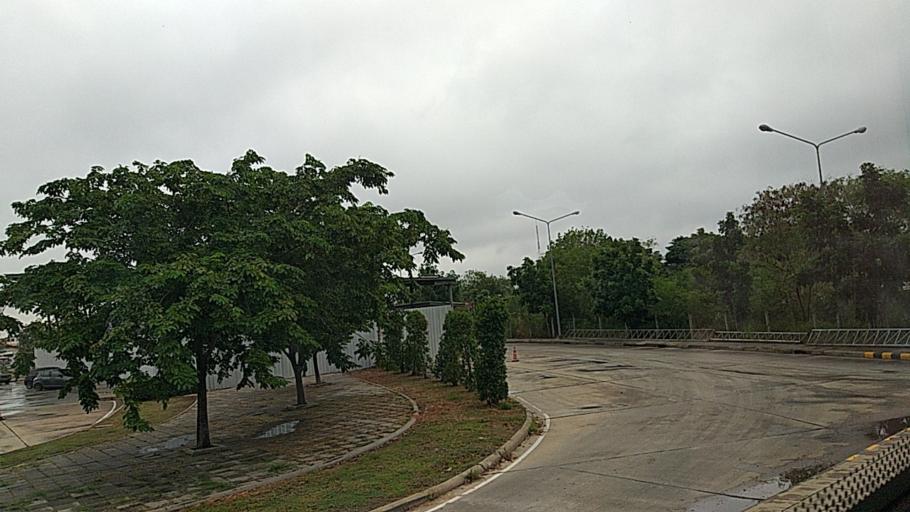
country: TH
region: Nakhon Ratchasima
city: Nakhon Ratchasima
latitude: 14.9914
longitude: 102.0926
